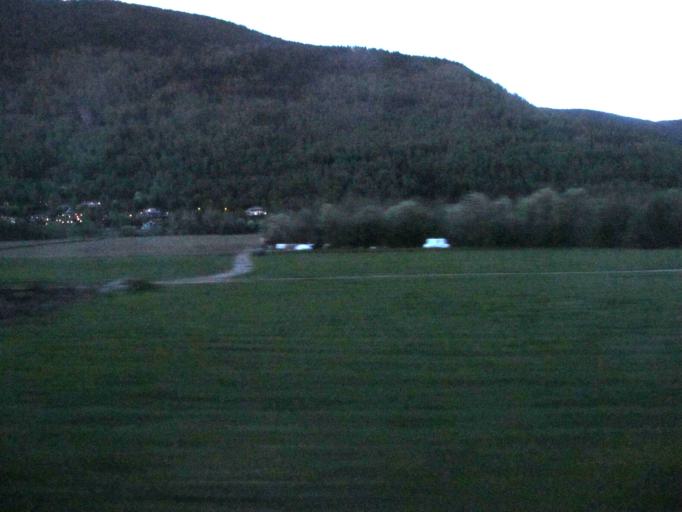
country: NO
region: Oppland
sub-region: Sel
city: Otta
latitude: 61.7593
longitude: 9.5357
